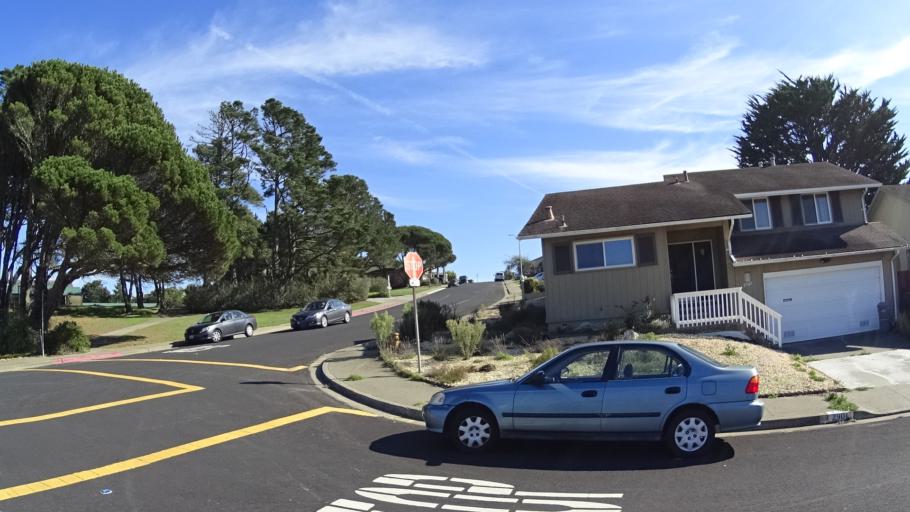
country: US
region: California
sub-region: San Mateo County
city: Colma
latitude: 37.6389
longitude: -122.4503
